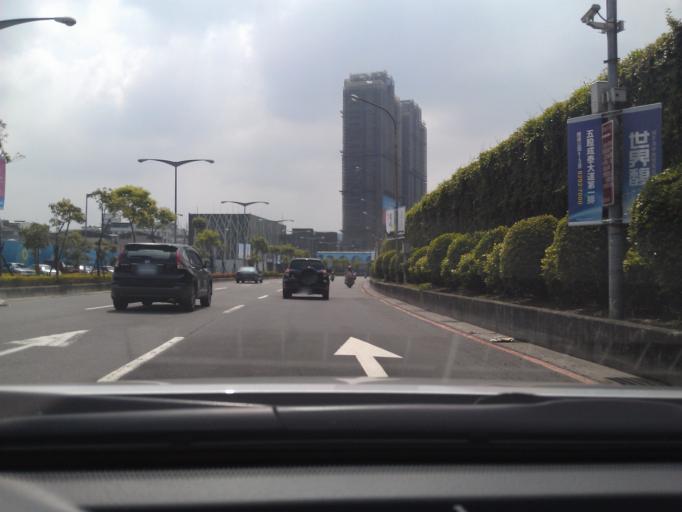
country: TW
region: Taipei
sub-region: Taipei
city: Banqiao
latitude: 25.0078
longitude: 121.4953
